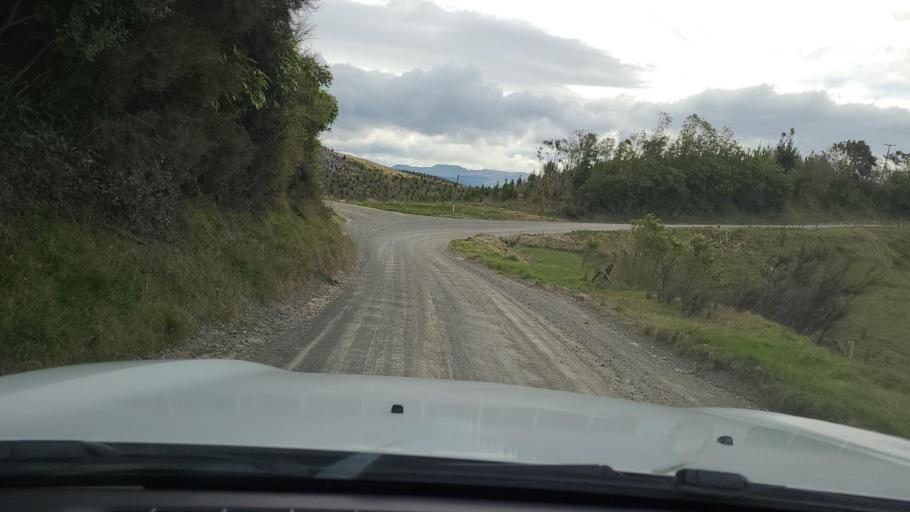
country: NZ
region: Hawke's Bay
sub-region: Napier City
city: Napier
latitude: -39.3370
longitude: 176.8295
